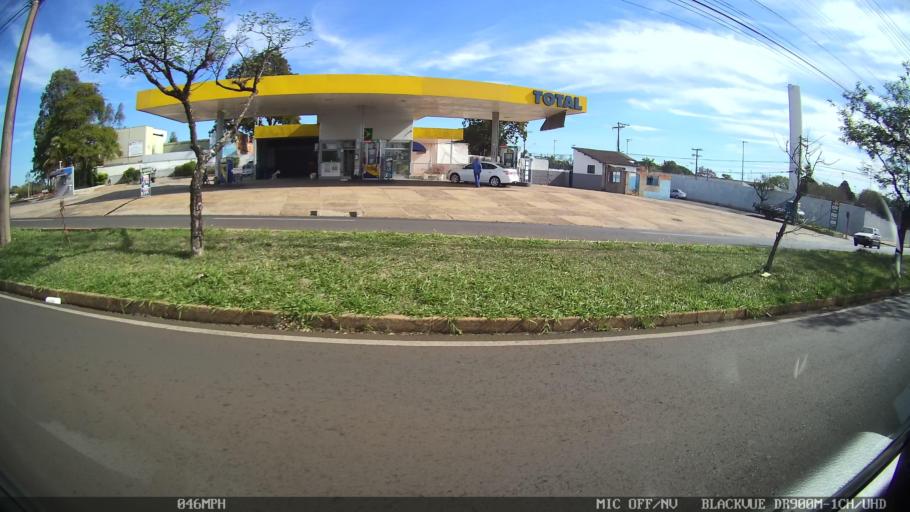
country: BR
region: Sao Paulo
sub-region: Araraquara
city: Araraquara
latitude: -21.8103
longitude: -48.1592
